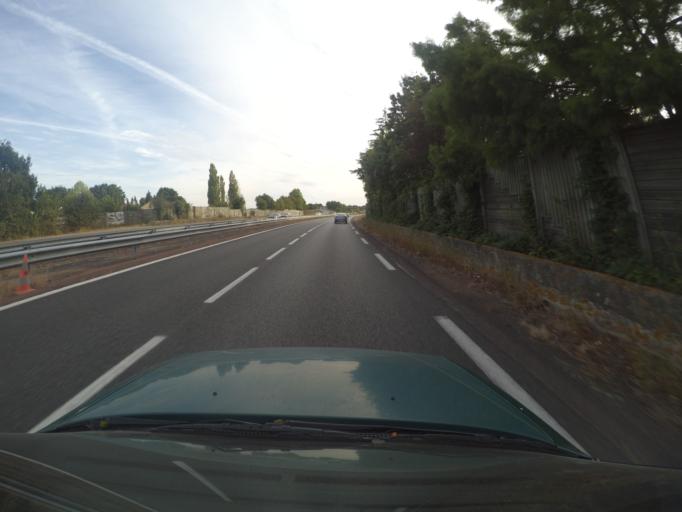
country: FR
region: Pays de la Loire
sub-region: Departement de la Vendee
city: Bouffere
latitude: 46.9240
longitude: -1.3663
